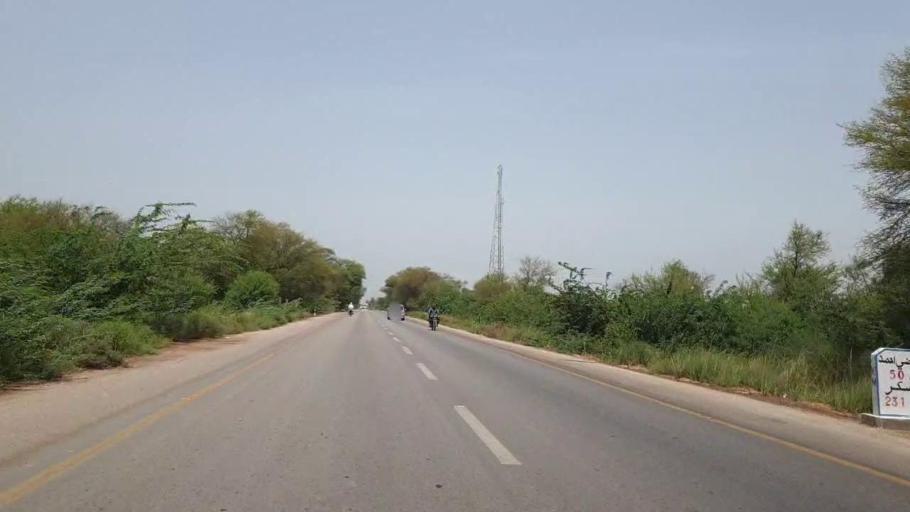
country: PK
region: Sindh
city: Nawabshah
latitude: 26.2107
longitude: 68.5207
